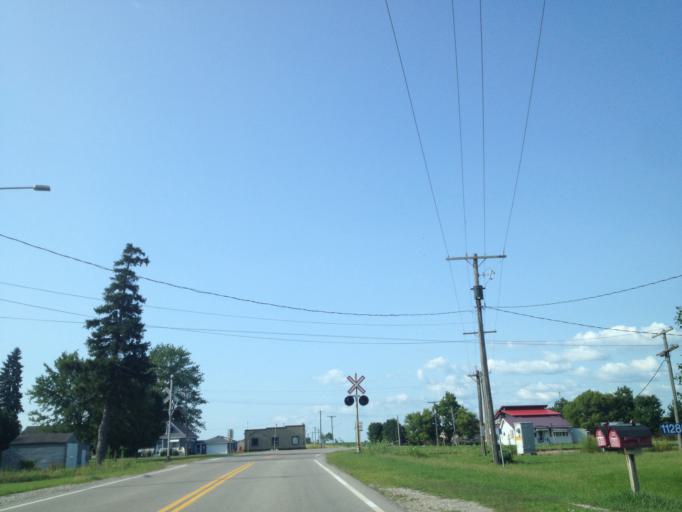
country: CA
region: Ontario
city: Aylmer
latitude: 42.8207
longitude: -80.8321
